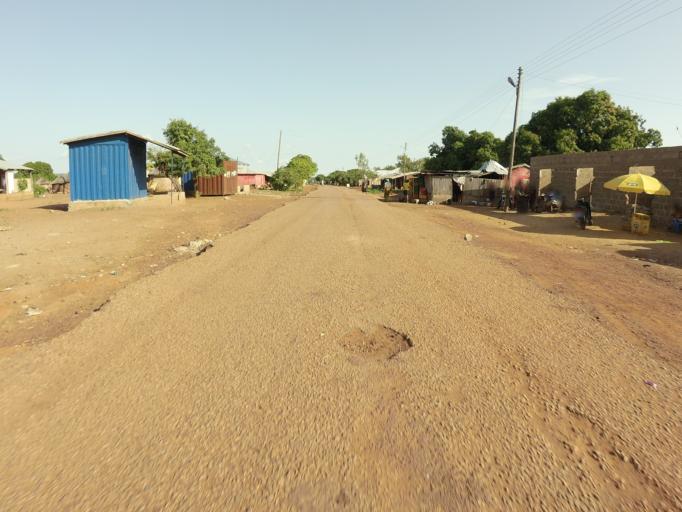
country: GH
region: Upper East
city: Bawku
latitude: 10.6309
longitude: -0.1804
